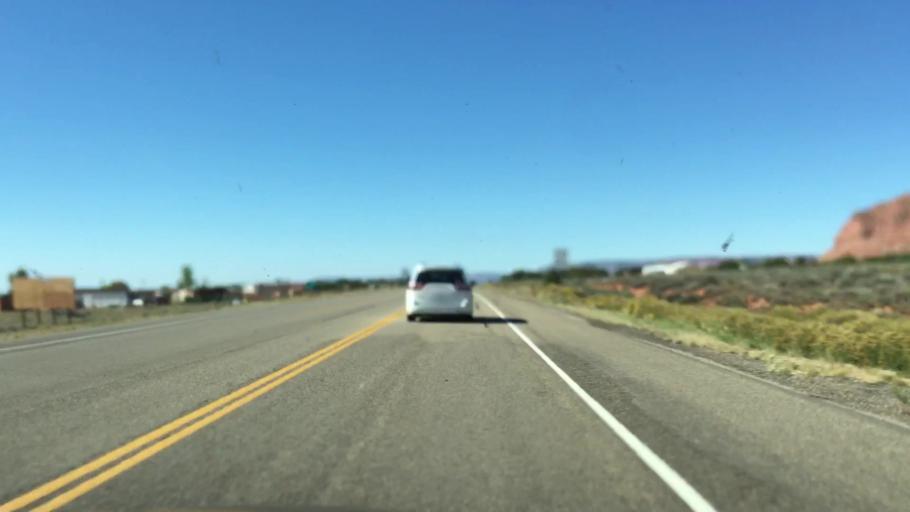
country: US
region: Utah
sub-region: Kane County
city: Kanab
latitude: 37.0269
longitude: -112.4173
